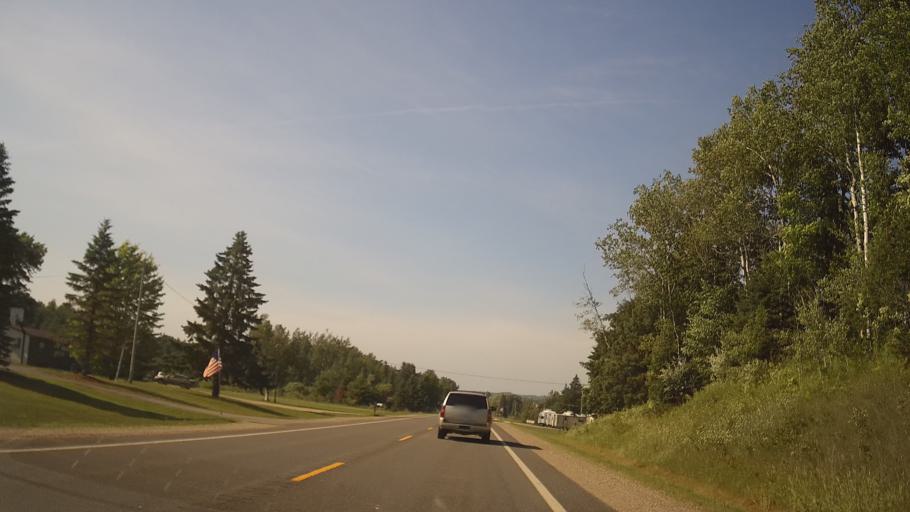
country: US
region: Michigan
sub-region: Ogemaw County
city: West Branch
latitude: 44.3980
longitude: -84.1164
